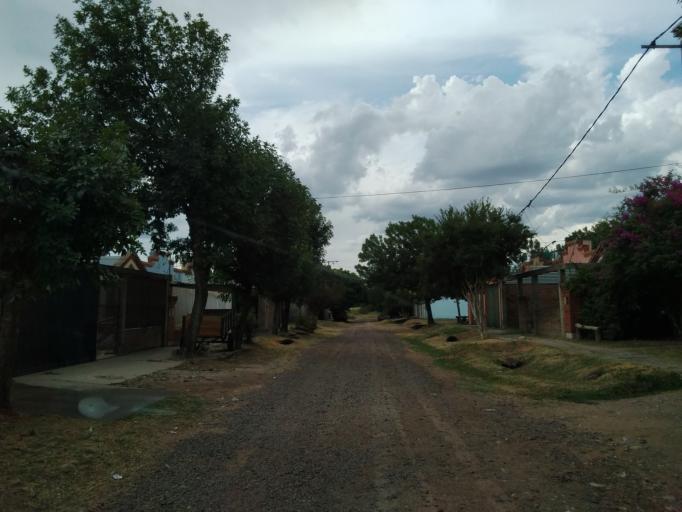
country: AR
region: Corrientes
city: Corrientes
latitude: -27.5188
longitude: -58.7903
